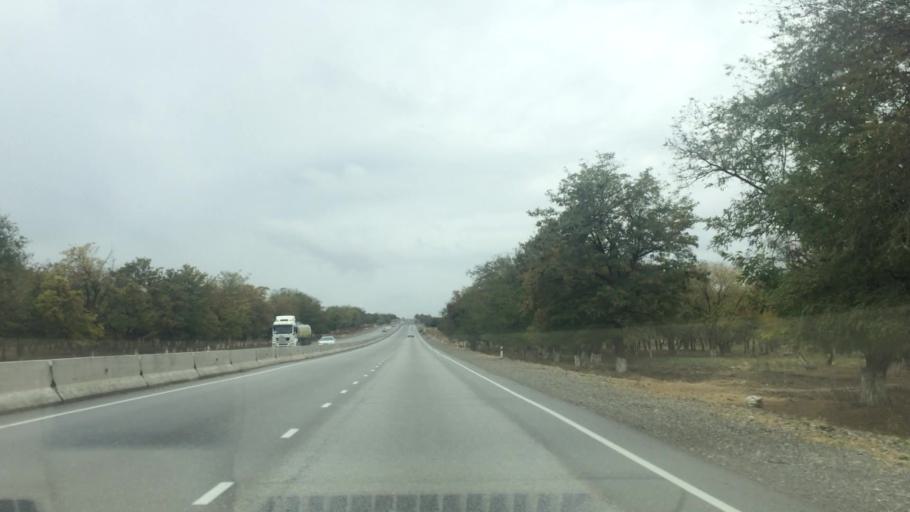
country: UZ
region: Samarqand
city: Bulung'ur
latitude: 39.8696
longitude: 67.4770
